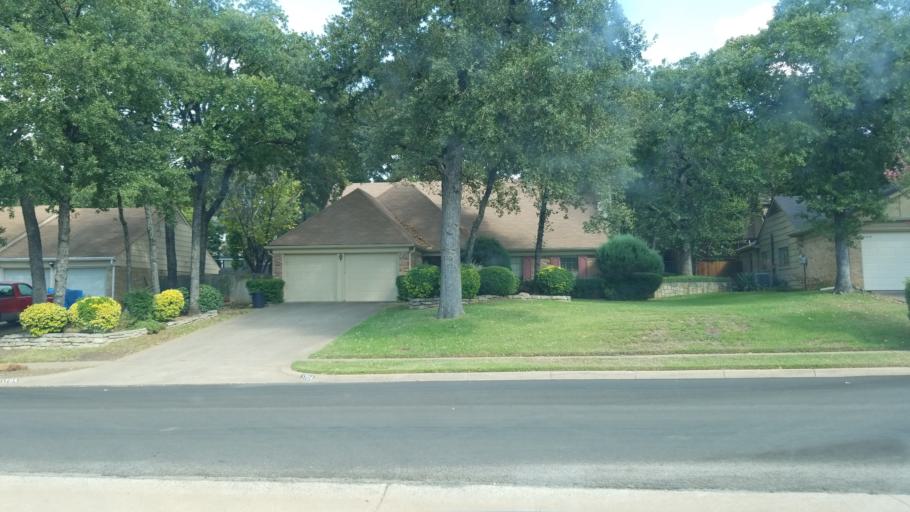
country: US
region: Texas
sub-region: Tarrant County
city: Euless
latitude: 32.8607
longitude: -97.0755
